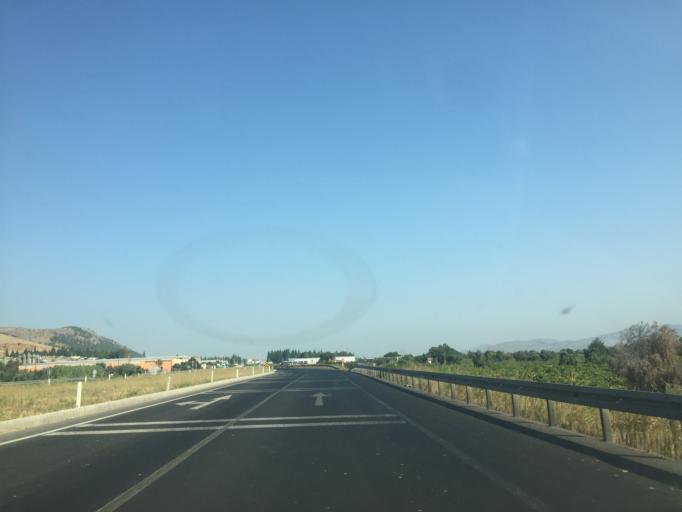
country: TR
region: Manisa
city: Golmarmara
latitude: 38.6936
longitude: 27.9339
